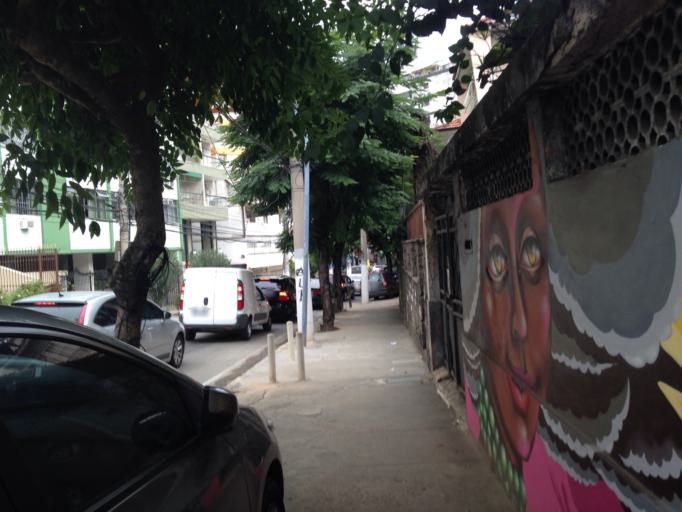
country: BR
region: Rio de Janeiro
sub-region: Niteroi
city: Niteroi
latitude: -22.9011
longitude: -43.1212
